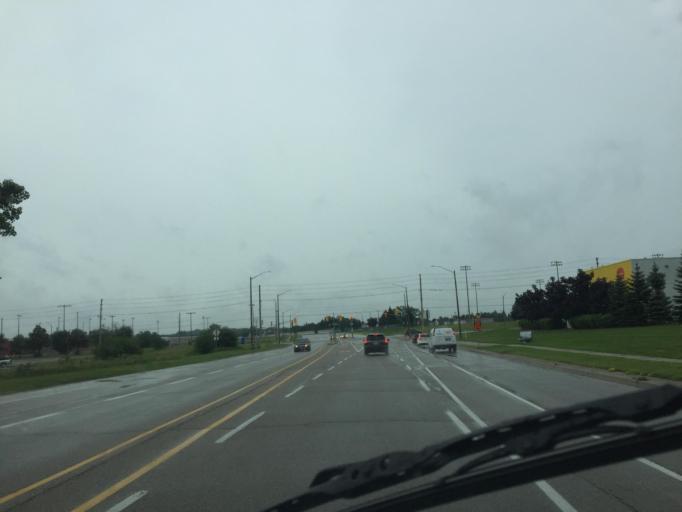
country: CA
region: Ontario
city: Cambridge
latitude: 43.3935
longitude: -80.3051
